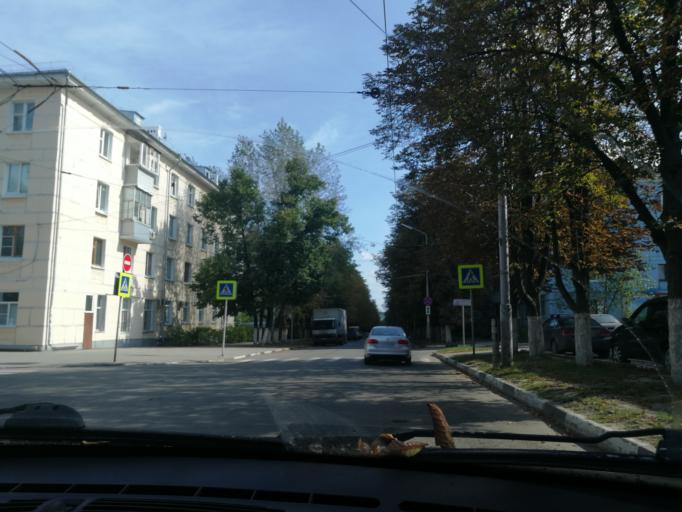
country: RU
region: Rjazan
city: Ryazan'
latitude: 54.6092
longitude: 39.7183
